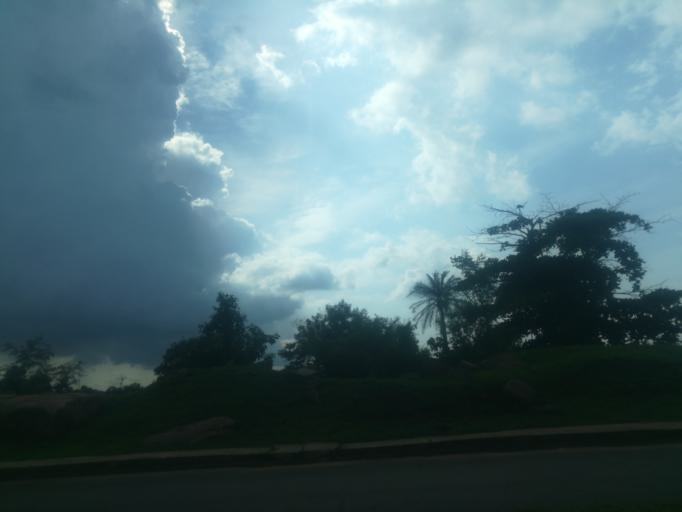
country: NG
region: Oyo
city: Ibadan
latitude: 7.4529
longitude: 3.8990
